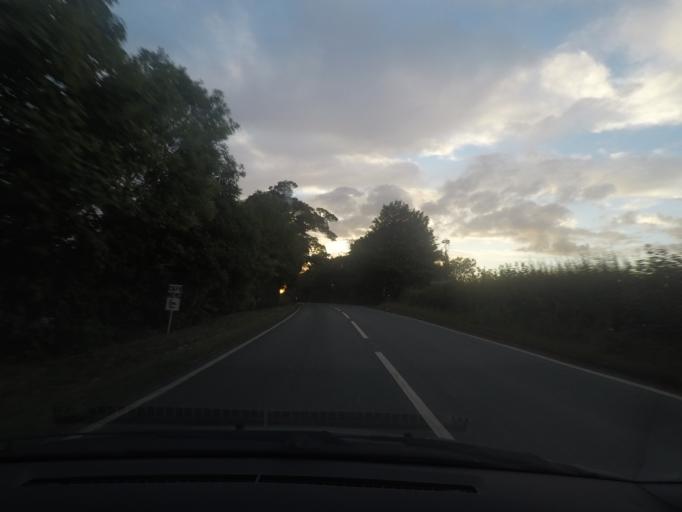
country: GB
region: England
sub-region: North Lincolnshire
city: Croxton
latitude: 53.5853
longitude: -0.3558
